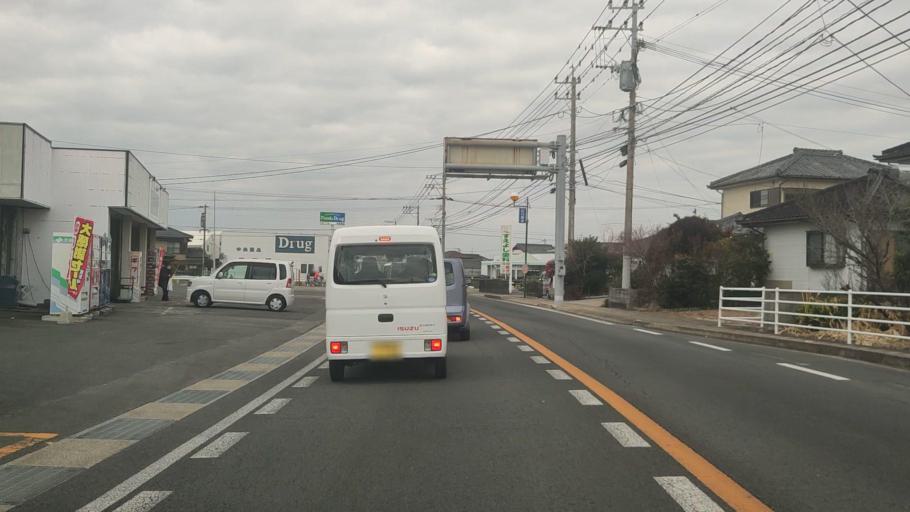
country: JP
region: Nagasaki
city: Shimabara
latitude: 32.8560
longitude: 130.3376
